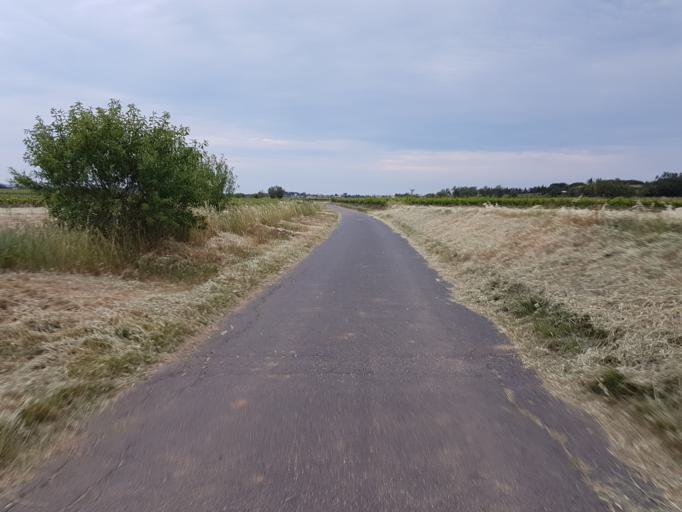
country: FR
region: Languedoc-Roussillon
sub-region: Departement de l'Herault
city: Cers
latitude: 43.3205
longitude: 3.3169
